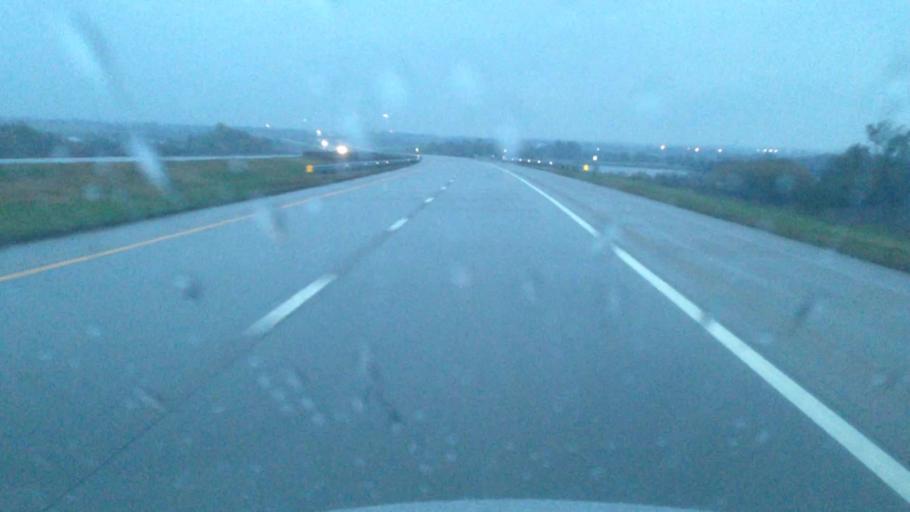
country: US
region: Kansas
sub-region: Franklin County
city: Ottawa
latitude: 38.6735
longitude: -95.2599
